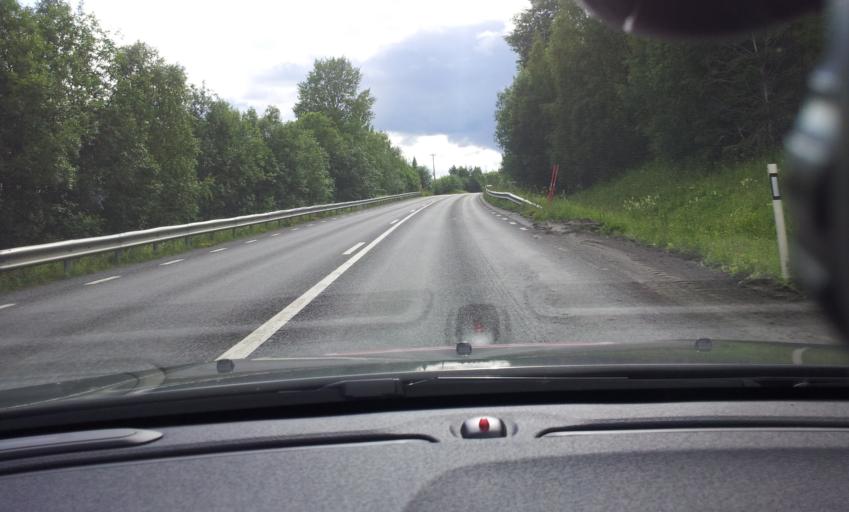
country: SE
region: Jaemtland
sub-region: Are Kommun
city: Jarpen
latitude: 63.3221
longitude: 13.3649
